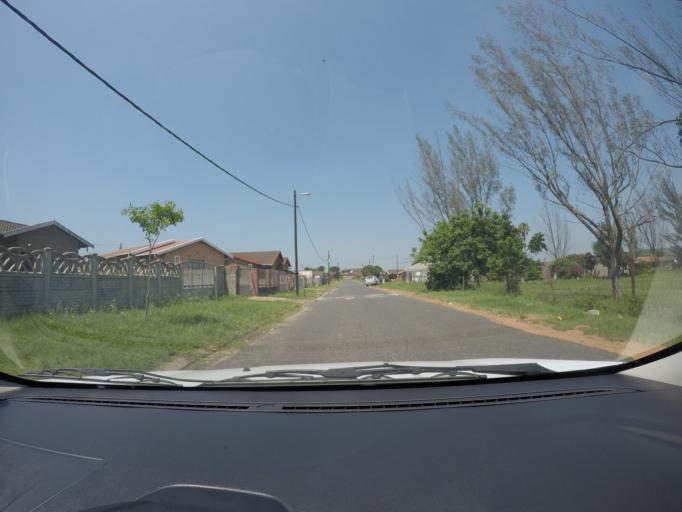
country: ZA
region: KwaZulu-Natal
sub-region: uThungulu District Municipality
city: eSikhawini
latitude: -28.8647
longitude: 31.9185
